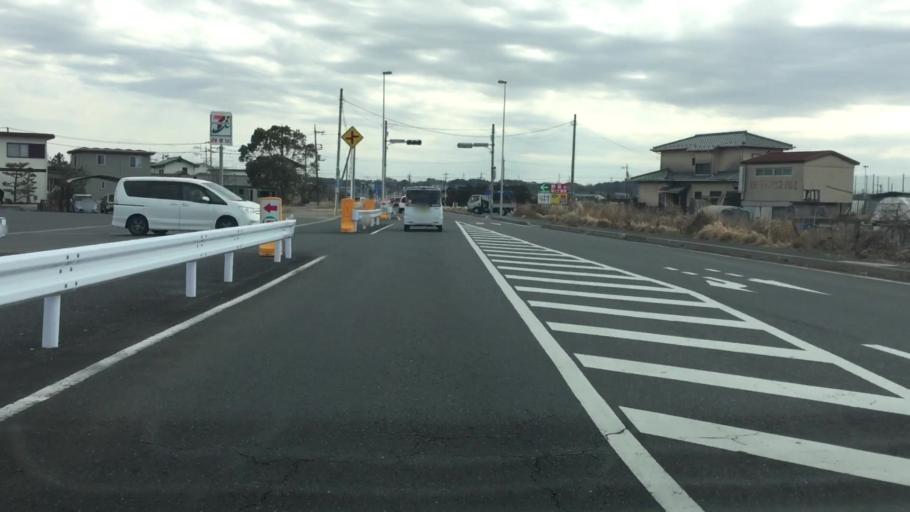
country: JP
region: Ibaraki
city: Fujishiro
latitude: 35.8474
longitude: 140.1310
